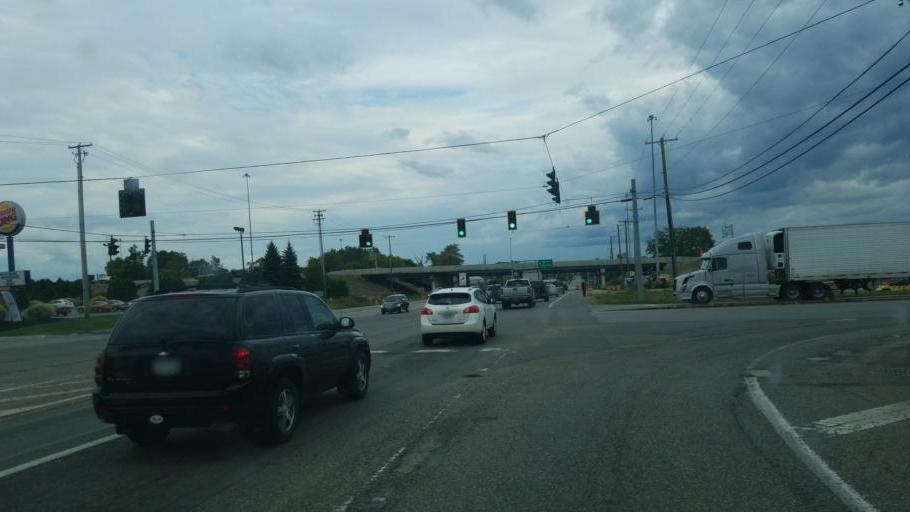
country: US
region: Ohio
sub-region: Trumbull County
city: Hubbard
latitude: 41.1781
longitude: -80.5686
